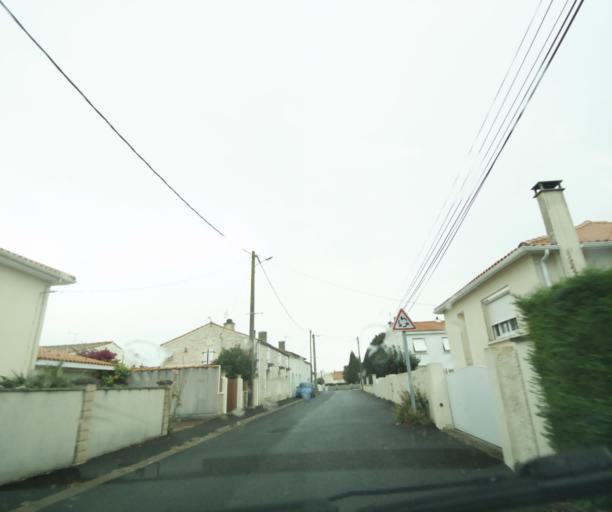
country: FR
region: Poitou-Charentes
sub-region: Departement de la Charente-Maritime
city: Tonnay-Charente
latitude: 45.9465
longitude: -0.9151
